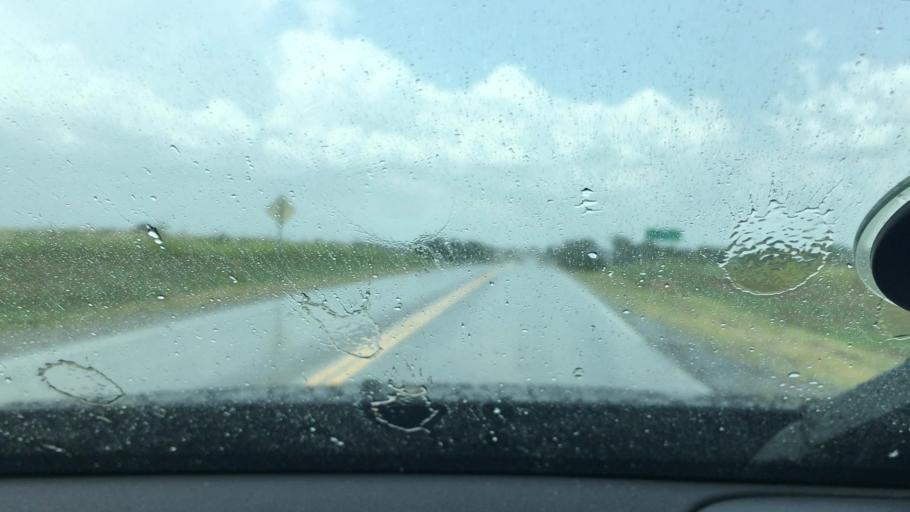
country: US
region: Oklahoma
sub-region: Johnston County
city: Tishomingo
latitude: 34.1731
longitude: -96.7133
